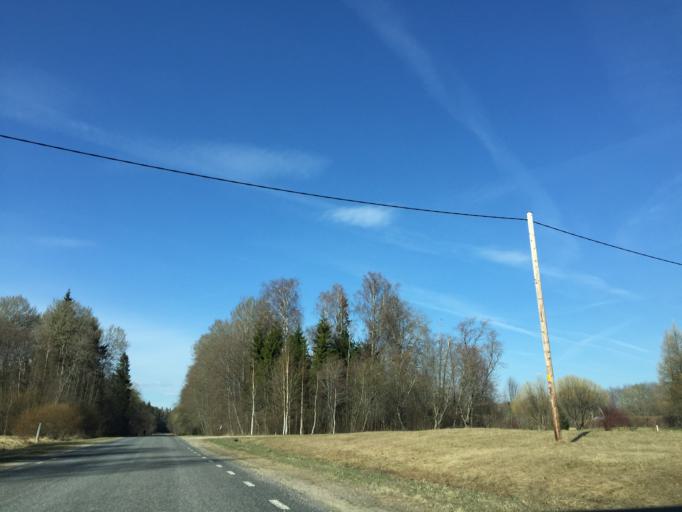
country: EE
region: Vorumaa
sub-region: Antsla vald
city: Vana-Antsla
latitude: 57.9995
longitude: 26.4238
